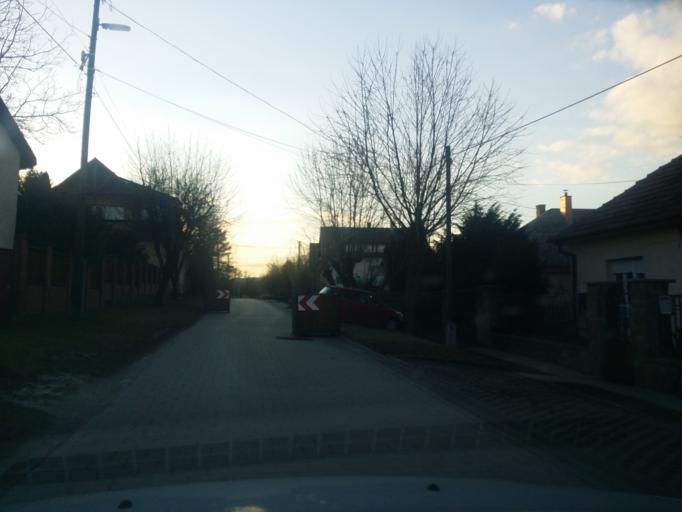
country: HU
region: Pest
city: Pilisvorosvar
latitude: 47.6174
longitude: 18.9198
